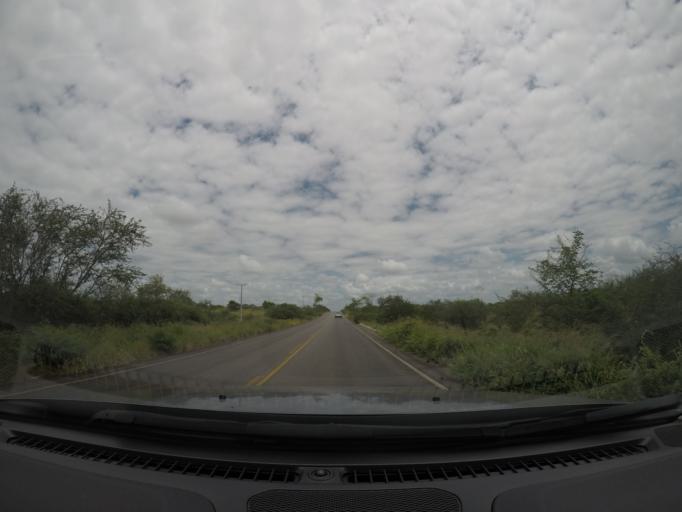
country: BR
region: Bahia
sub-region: Itaberaba
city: Itaberaba
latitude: -12.4812
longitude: -40.2109
